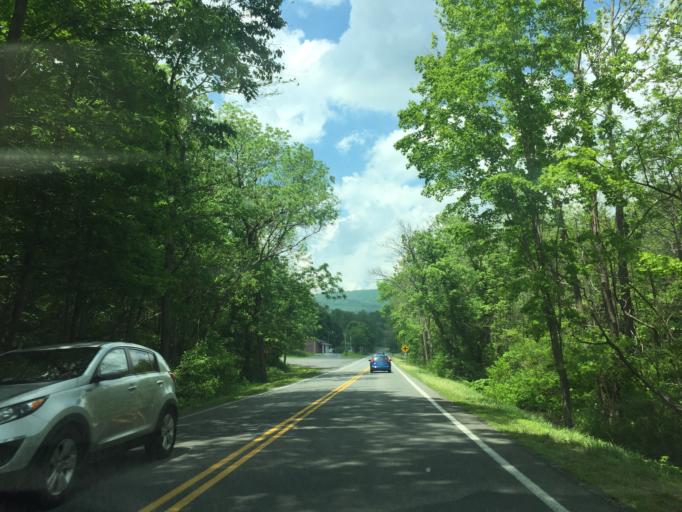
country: US
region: Virginia
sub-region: Shenandoah County
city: Strasburg
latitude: 39.0869
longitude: -78.4327
